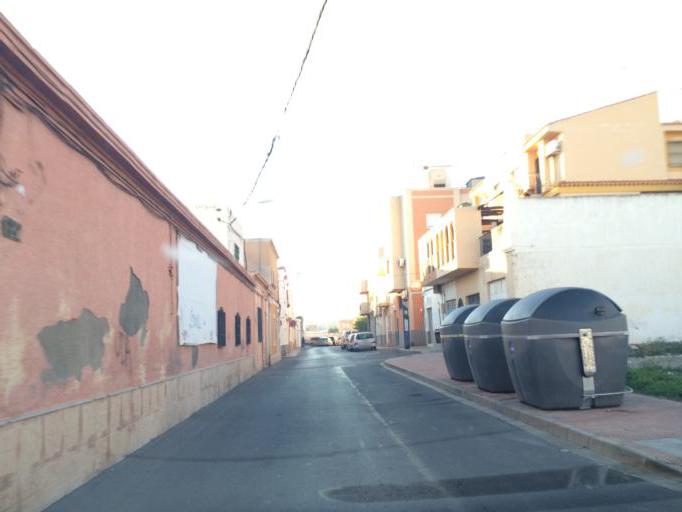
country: ES
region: Andalusia
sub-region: Provincia de Almeria
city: Almeria
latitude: 36.8506
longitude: -2.4367
